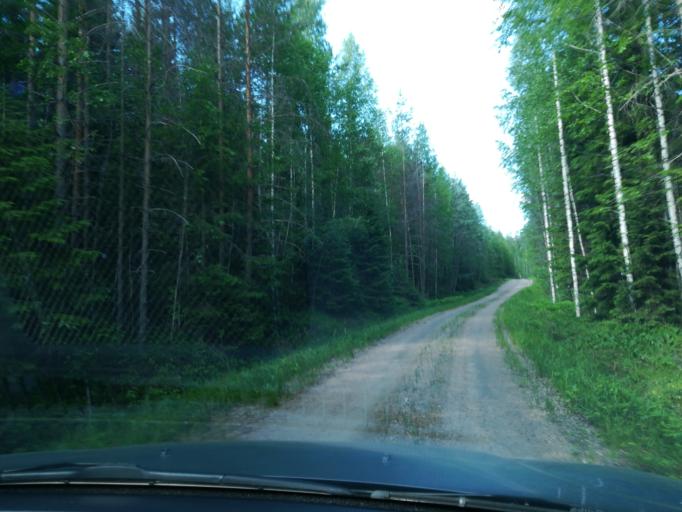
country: FI
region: South Karelia
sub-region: Imatra
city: Ruokolahti
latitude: 61.5472
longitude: 28.8101
